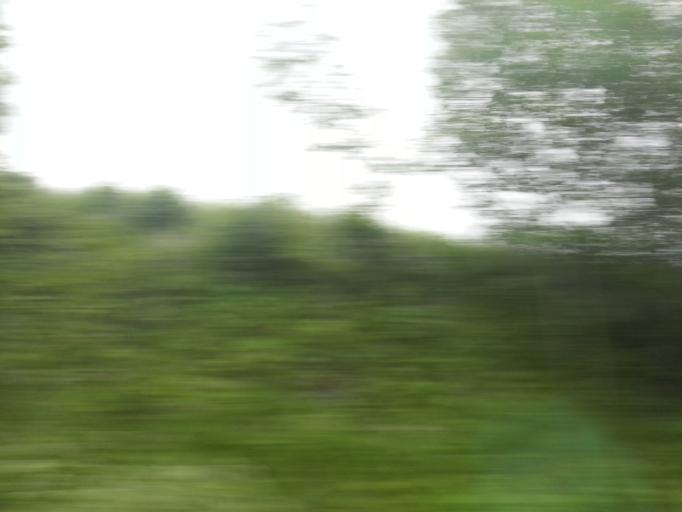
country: NO
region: Sor-Trondelag
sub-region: Trondheim
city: Trondheim
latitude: 63.3718
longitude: 10.3650
